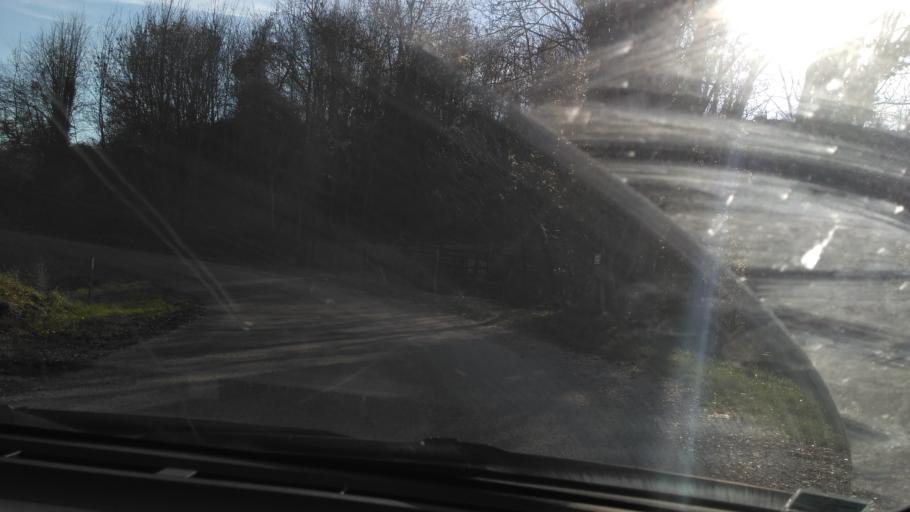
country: FR
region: Rhone-Alpes
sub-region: Departement de l'Isere
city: Saint-Antoine-l'Abbaye
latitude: 45.1480
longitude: 5.1427
